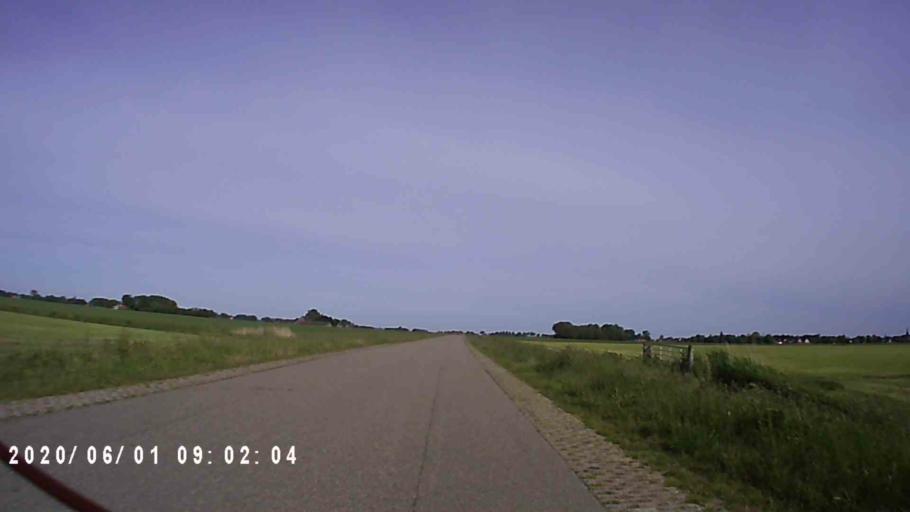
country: NL
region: Friesland
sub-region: Gemeente Ferwerderadiel
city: Hallum
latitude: 53.2921
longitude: 5.7871
